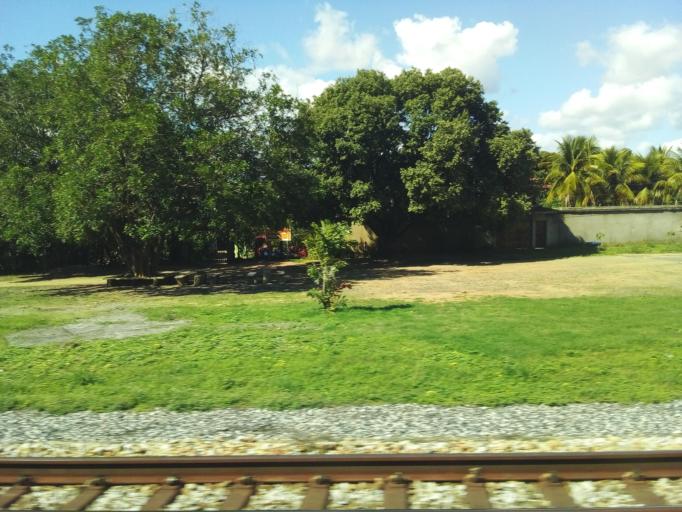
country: BR
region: Minas Gerais
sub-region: Governador Valadares
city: Governador Valadares
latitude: -18.8608
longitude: -41.8617
